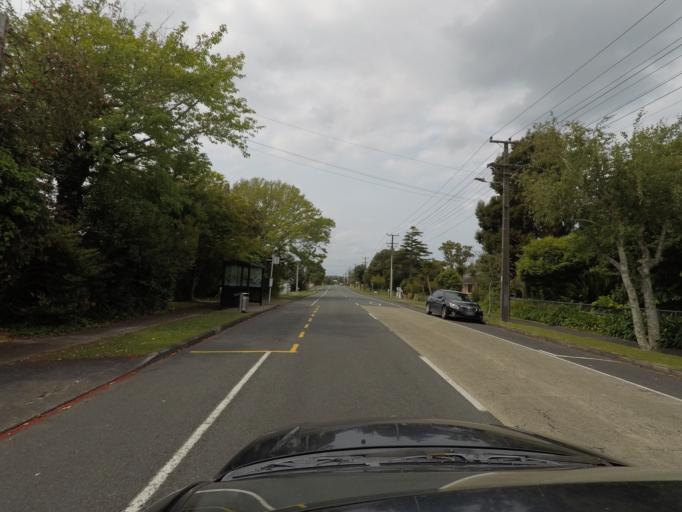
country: NZ
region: Auckland
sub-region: Auckland
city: Rosebank
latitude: -36.8373
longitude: 174.6420
